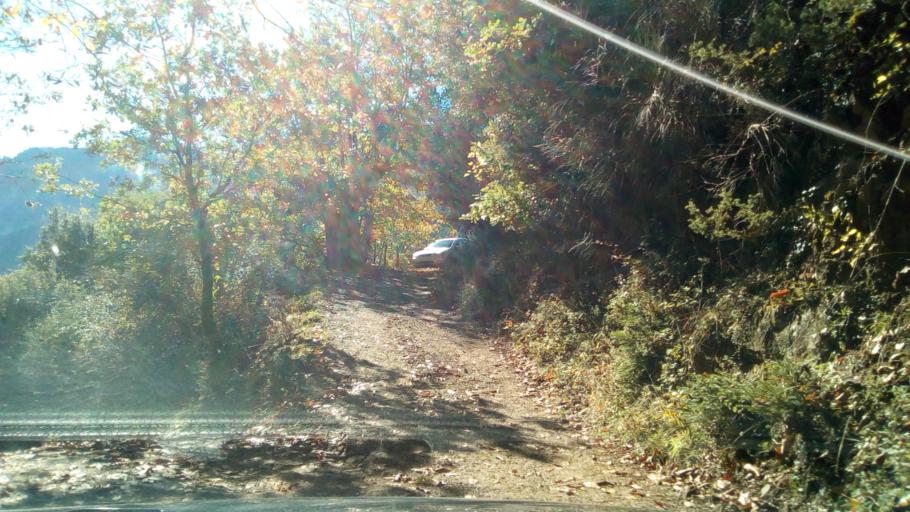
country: GR
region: West Greece
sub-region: Nomos Aitolias kai Akarnanias
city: Nafpaktos
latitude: 38.5918
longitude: 21.8789
